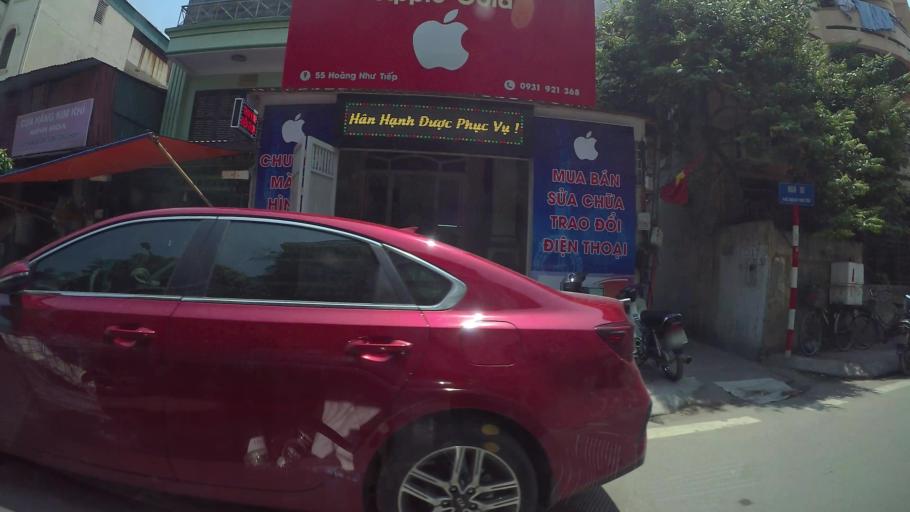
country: VN
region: Ha Noi
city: Hoan Kiem
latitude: 21.0422
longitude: 105.8764
